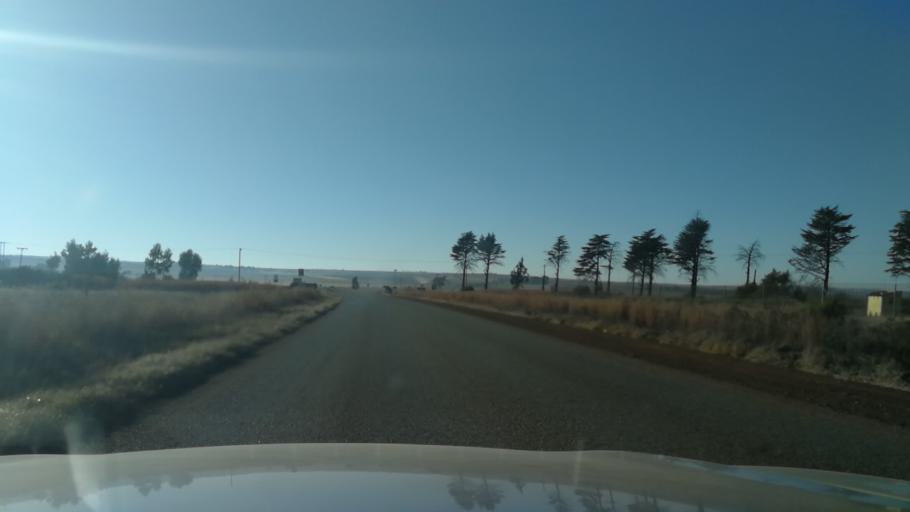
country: ZA
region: North-West
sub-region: Bojanala Platinum District Municipality
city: Rustenburg
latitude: -25.9716
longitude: 27.2338
